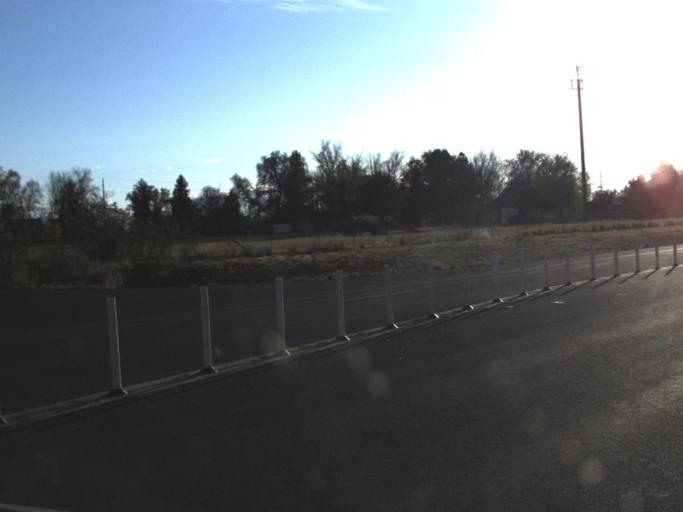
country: US
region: Washington
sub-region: Walla Walla County
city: Walla Walla
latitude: 46.0817
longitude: -118.3259
